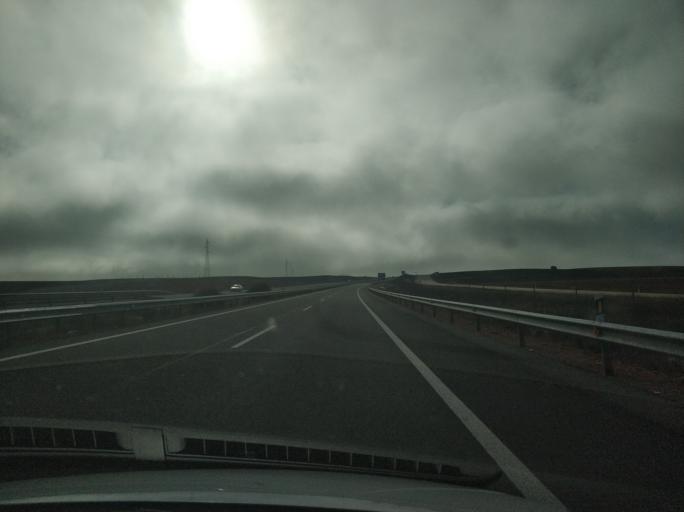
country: ES
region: Castille and Leon
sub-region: Provincia de Soria
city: Alcubilla de las Penas
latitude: 41.2788
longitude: -2.4754
